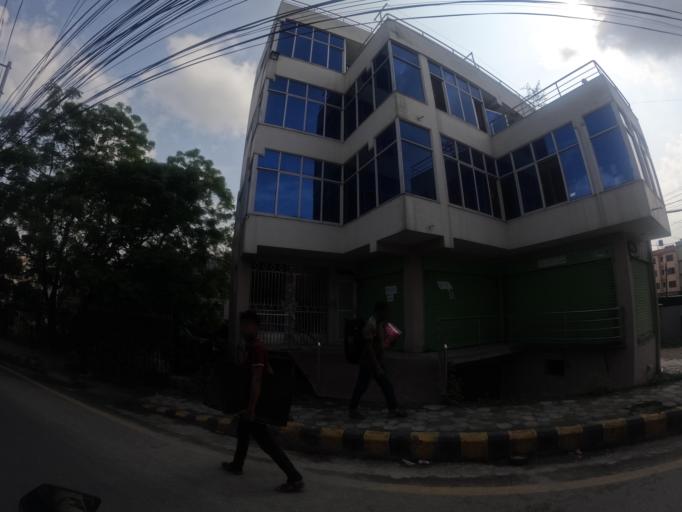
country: NP
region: Central Region
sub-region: Bagmati Zone
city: Patan
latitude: 27.6699
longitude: 85.3659
